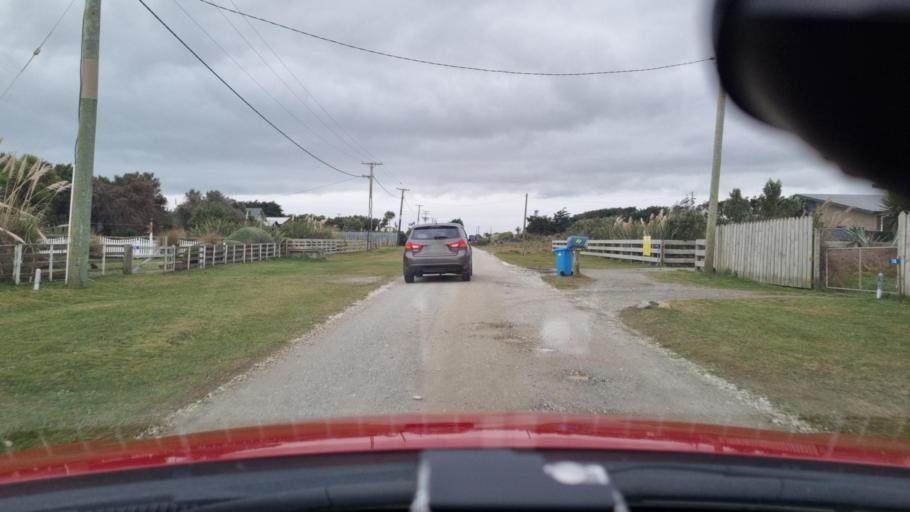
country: NZ
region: Southland
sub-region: Invercargill City
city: Invercargill
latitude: -46.4319
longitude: 168.2341
